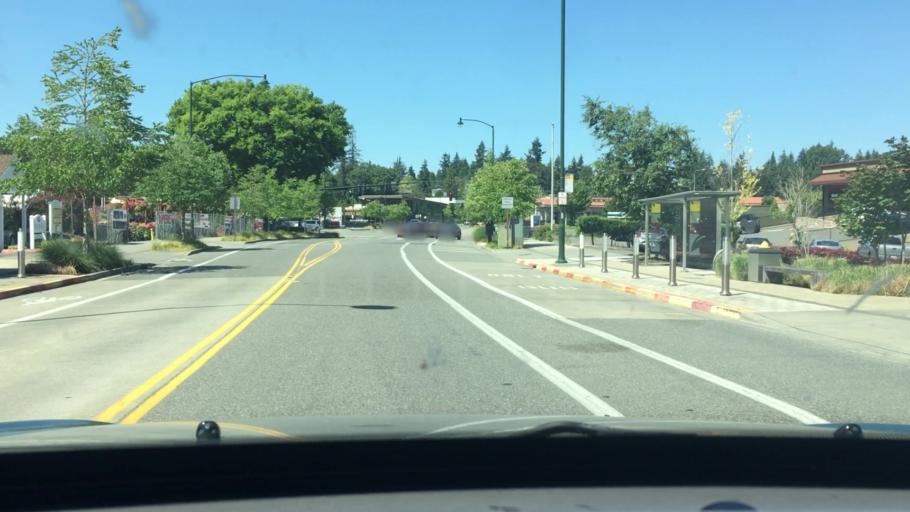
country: US
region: Washington
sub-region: King County
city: Newcastle
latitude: 47.5376
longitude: -122.1638
